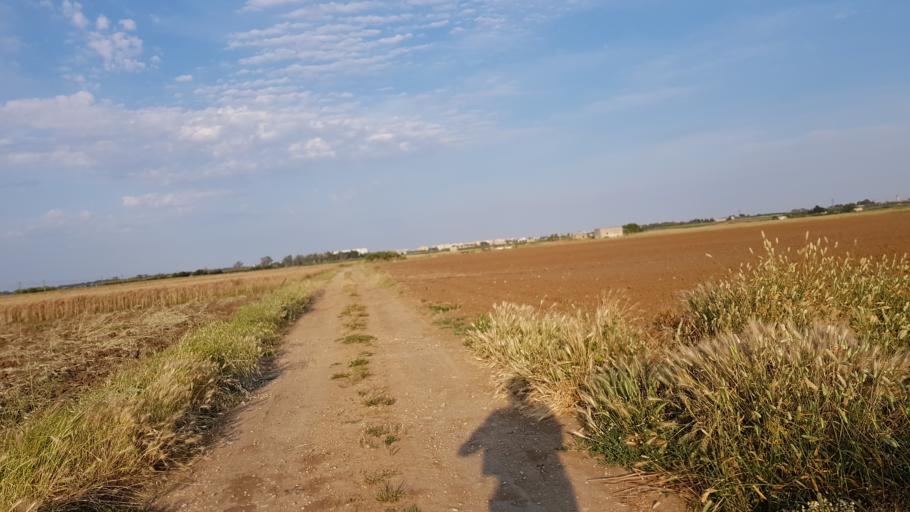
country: IT
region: Apulia
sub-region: Provincia di Brindisi
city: Brindisi
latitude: 40.6250
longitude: 17.8825
